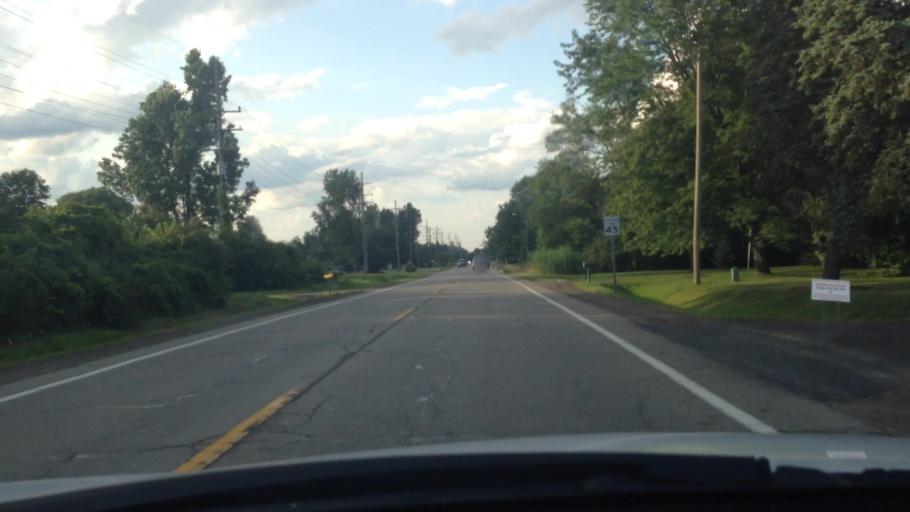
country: US
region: Michigan
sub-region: Wayne County
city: Flat Rock
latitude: 42.1618
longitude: -83.3055
